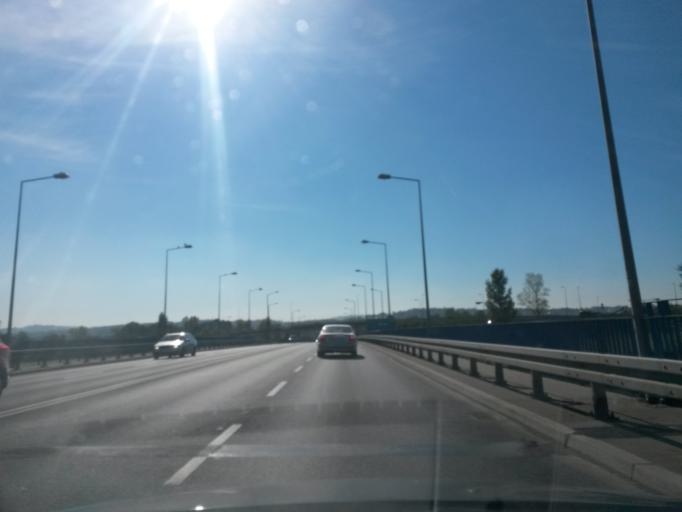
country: PL
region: Lesser Poland Voivodeship
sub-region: Powiat krakowski
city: Libertow
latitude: 49.9930
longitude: 19.9174
